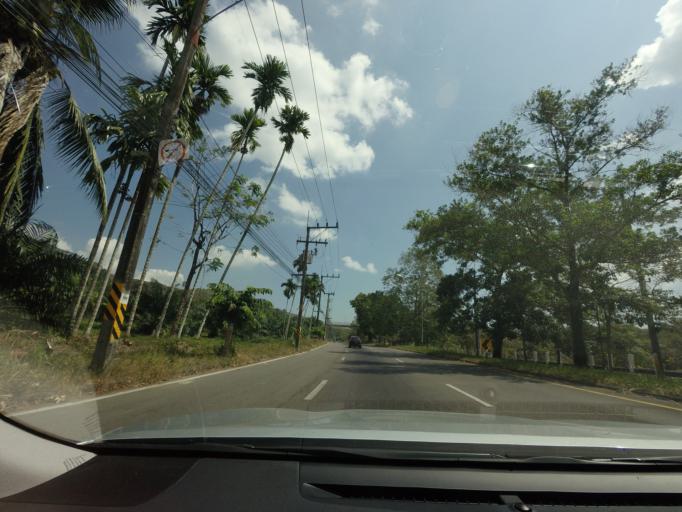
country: TH
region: Phangnga
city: Thai Mueang
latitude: 8.2711
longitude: 98.3312
